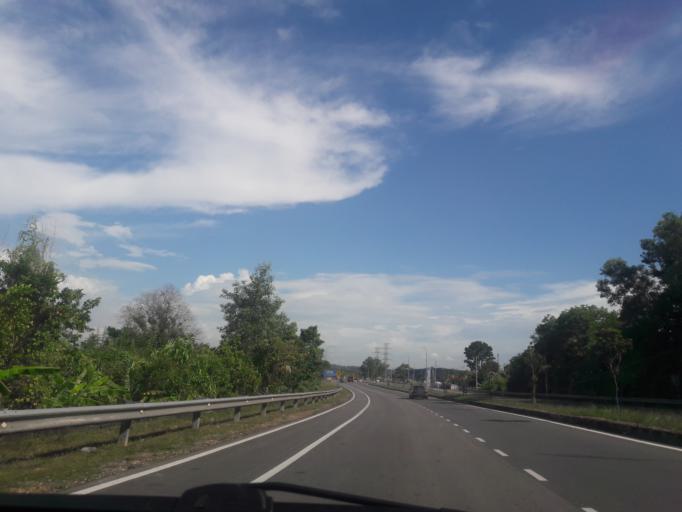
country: MY
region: Kedah
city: Sungai Petani
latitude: 5.6200
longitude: 100.4653
